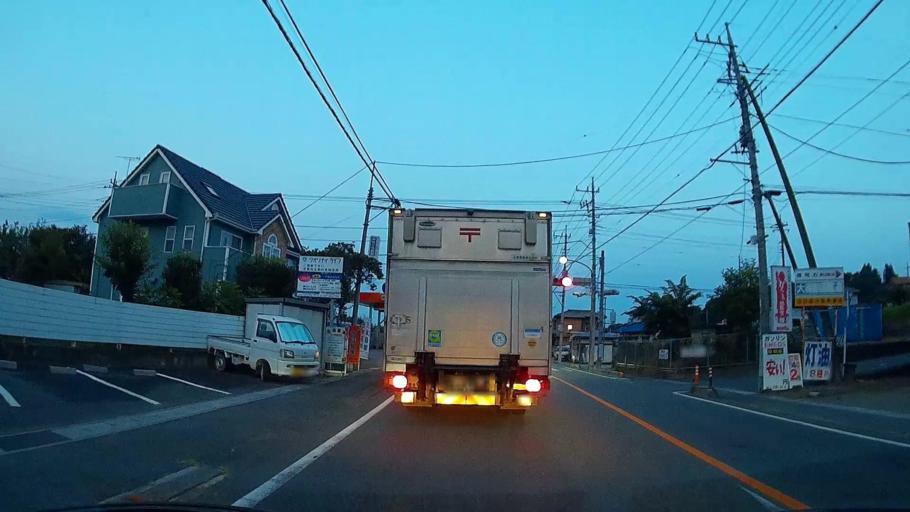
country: JP
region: Gunma
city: Annaka
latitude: 36.3603
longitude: 138.9187
